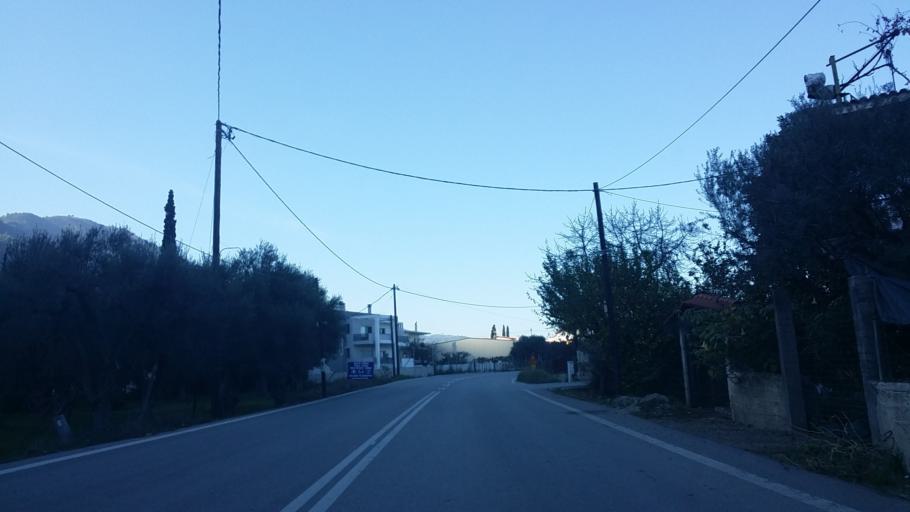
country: GR
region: West Greece
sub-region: Nomos Achaias
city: Temeni
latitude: 38.1839
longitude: 22.2018
